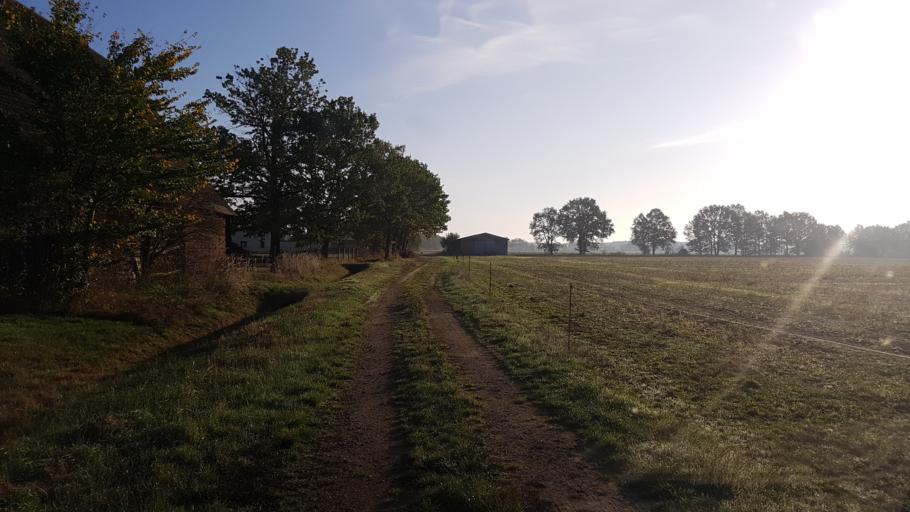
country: DE
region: Brandenburg
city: Ruckersdorf
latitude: 51.5945
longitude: 13.6101
